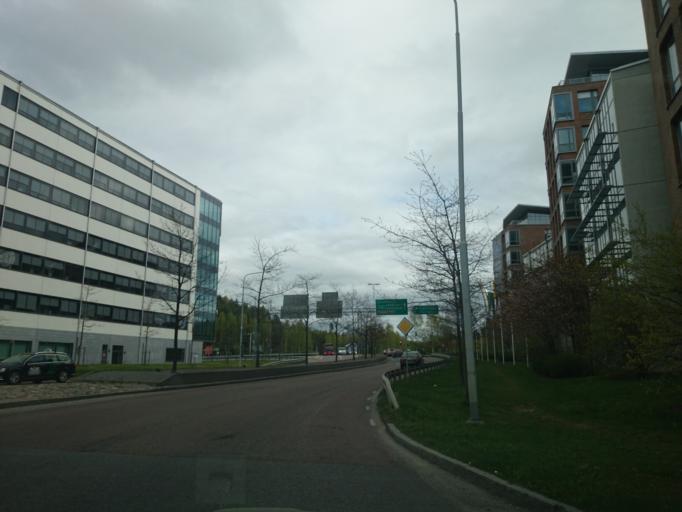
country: SE
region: Stockholm
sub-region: Solna Kommun
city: Solna
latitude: 59.3638
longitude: 18.0205
